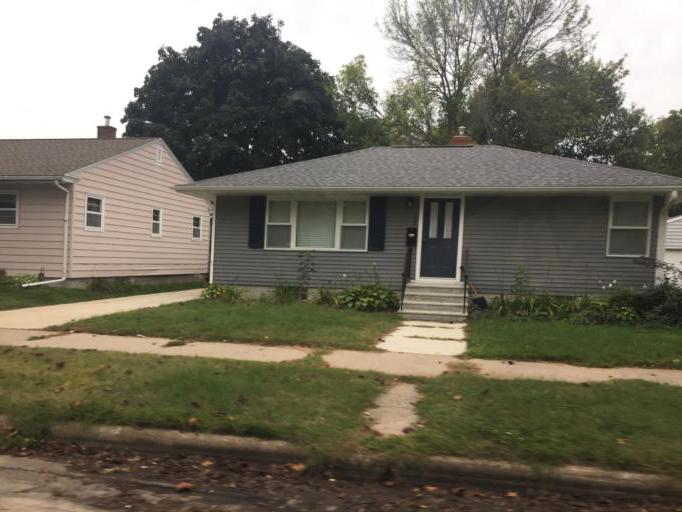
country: US
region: Minnesota
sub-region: Winona County
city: Winona
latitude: 44.0482
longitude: -91.6573
